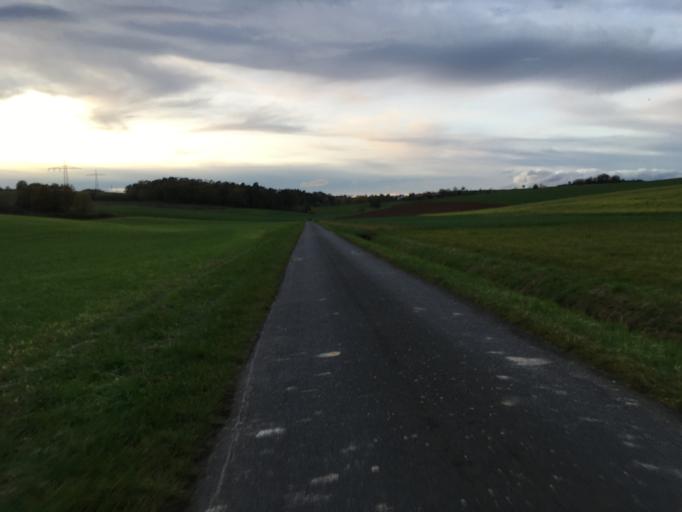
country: DE
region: Baden-Wuerttemberg
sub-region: Karlsruhe Region
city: Rosenberg
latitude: 49.3919
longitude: 9.4918
